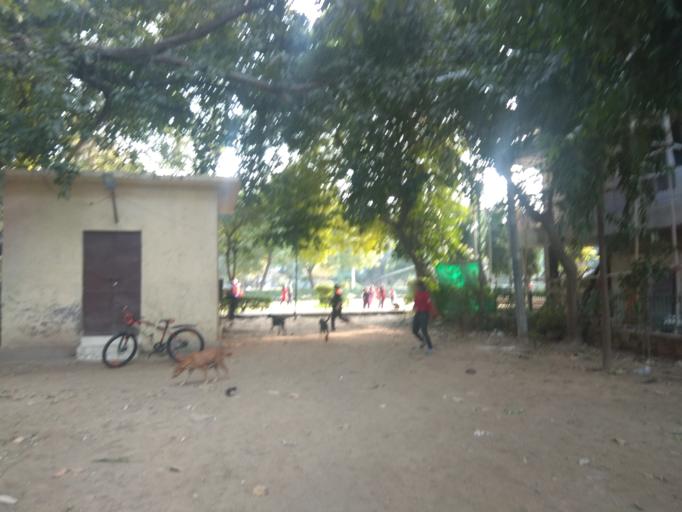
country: IN
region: NCT
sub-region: West Delhi
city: Nangloi Jat
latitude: 28.6282
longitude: 77.0669
